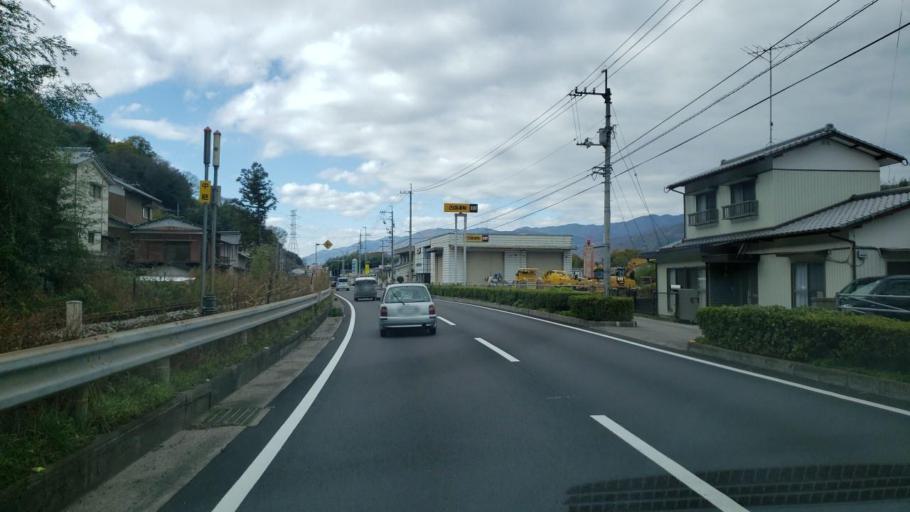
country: JP
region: Tokushima
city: Wakimachi
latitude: 34.0547
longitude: 134.1397
